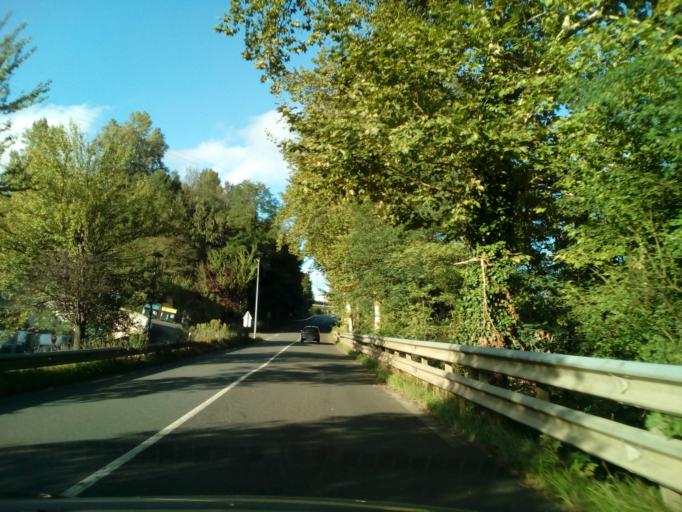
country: ES
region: Basque Country
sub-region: Provincia de Guipuzcoa
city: Urnieta
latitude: 43.2302
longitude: -2.0031
